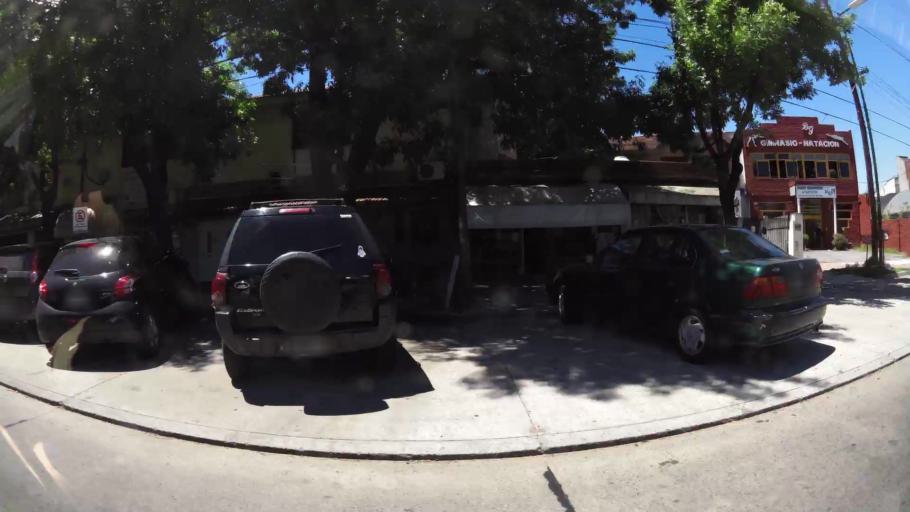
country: AR
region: Buenos Aires
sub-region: Partido de San Isidro
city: San Isidro
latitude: -34.4979
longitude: -58.5596
